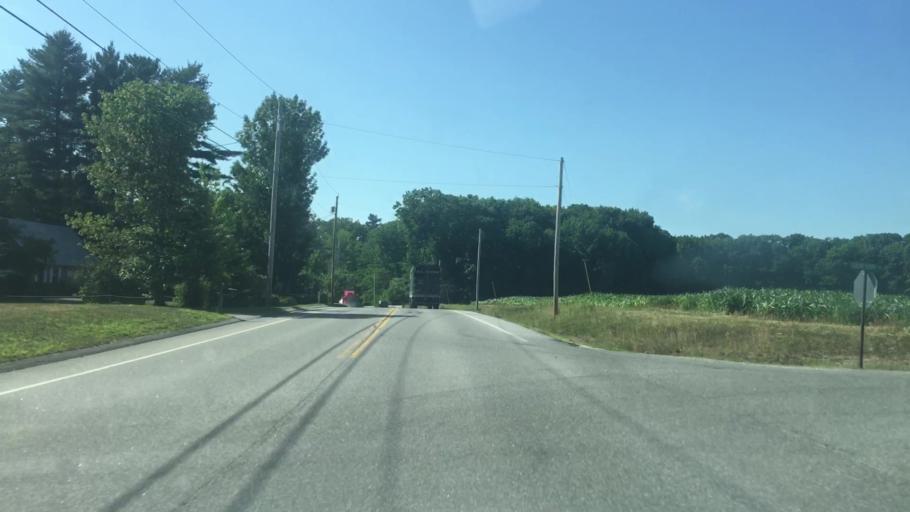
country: US
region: Maine
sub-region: York County
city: Buxton
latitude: 43.5942
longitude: -70.5277
